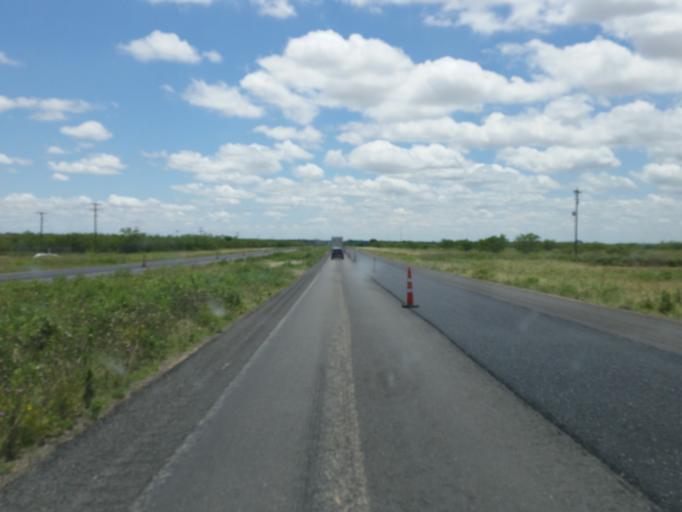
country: US
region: Texas
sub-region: Scurry County
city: Snyder
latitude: 32.7717
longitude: -100.9391
